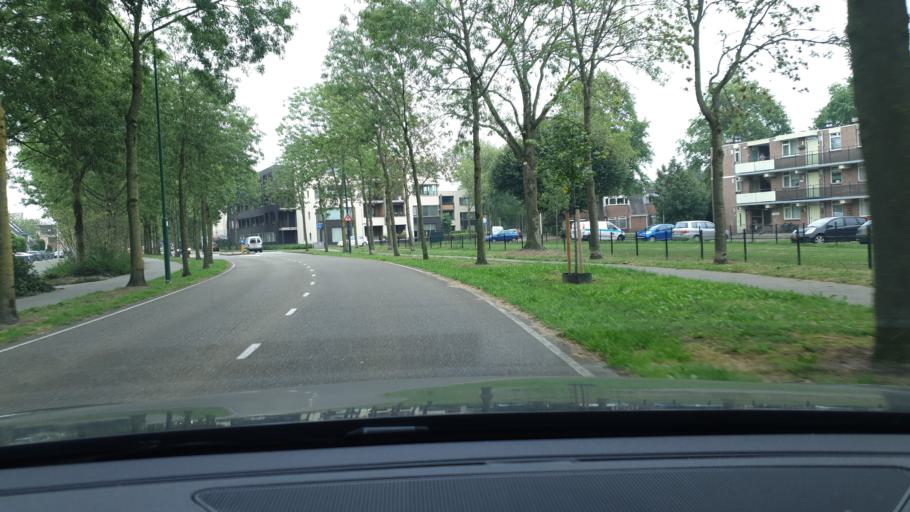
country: NL
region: North Brabant
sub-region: Gemeente Oss
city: Oss
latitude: 51.7708
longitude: 5.5036
